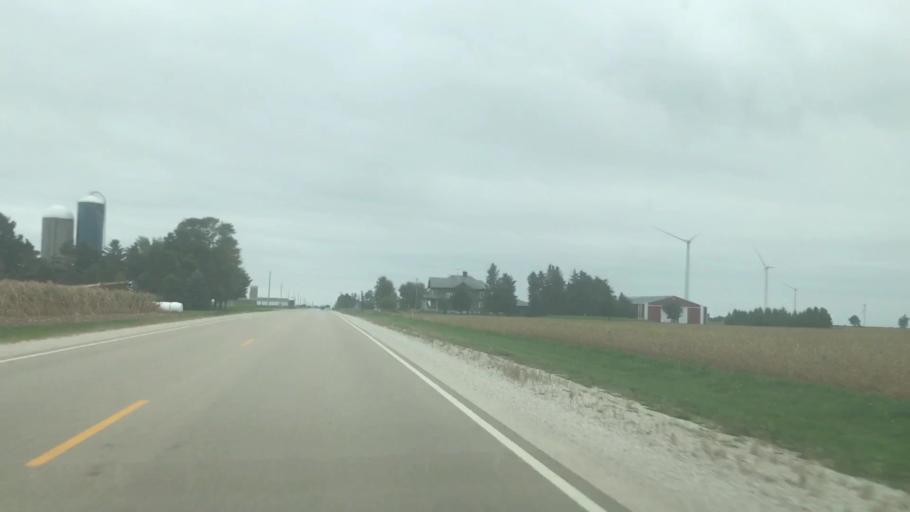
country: US
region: Wisconsin
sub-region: Fond du Lac County
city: Oakfield
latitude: 43.6284
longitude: -88.5417
